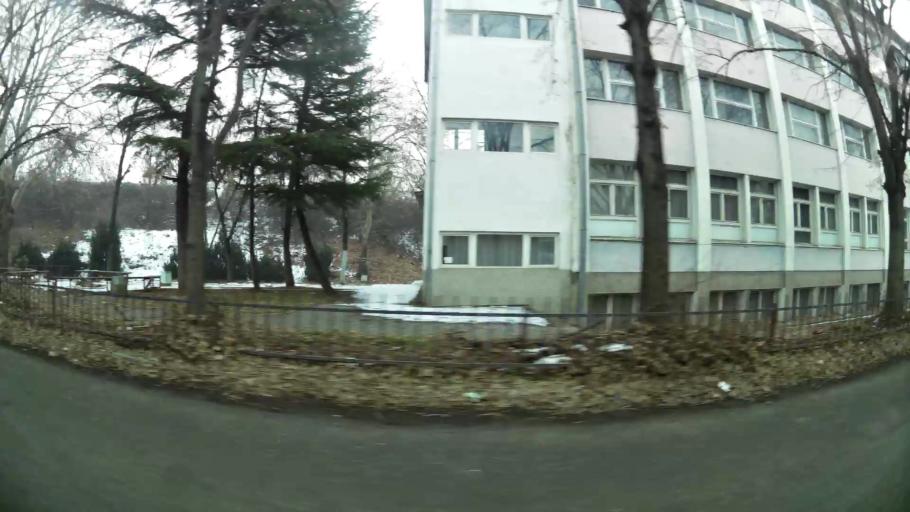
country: MK
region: Cair
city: Cair
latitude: 42.0064
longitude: 21.4654
